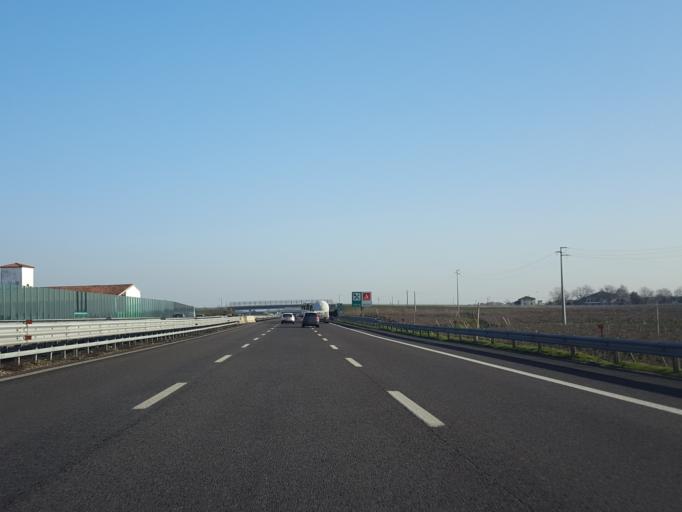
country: IT
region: Veneto
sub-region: Provincia di Verona
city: Caldiero
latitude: 45.4135
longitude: 11.2072
